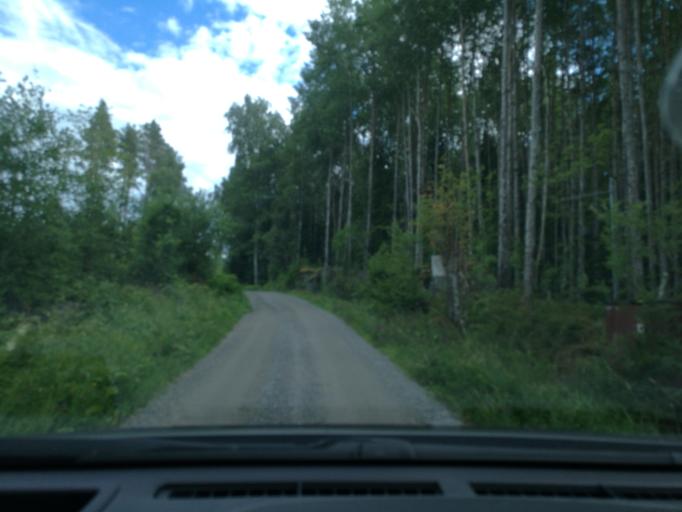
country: SE
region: Vaestmanland
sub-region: Surahammars Kommun
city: Ramnas
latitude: 59.7917
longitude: 16.3054
